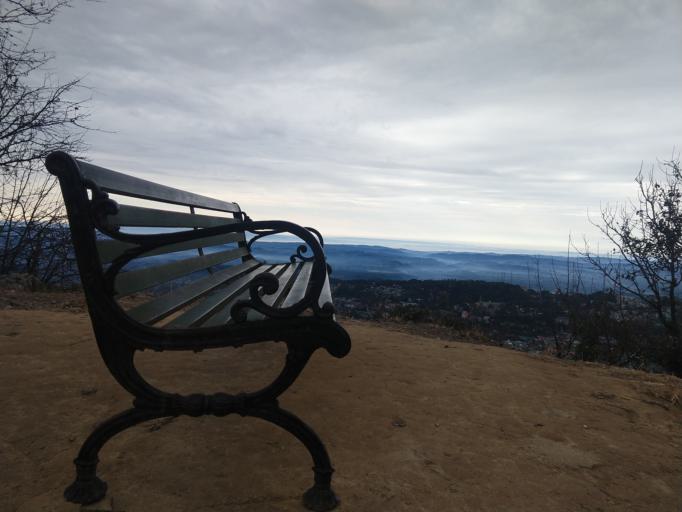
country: IN
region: Himachal Pradesh
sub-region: Kangra
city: Dharmsala
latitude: 32.2200
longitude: 76.3349
